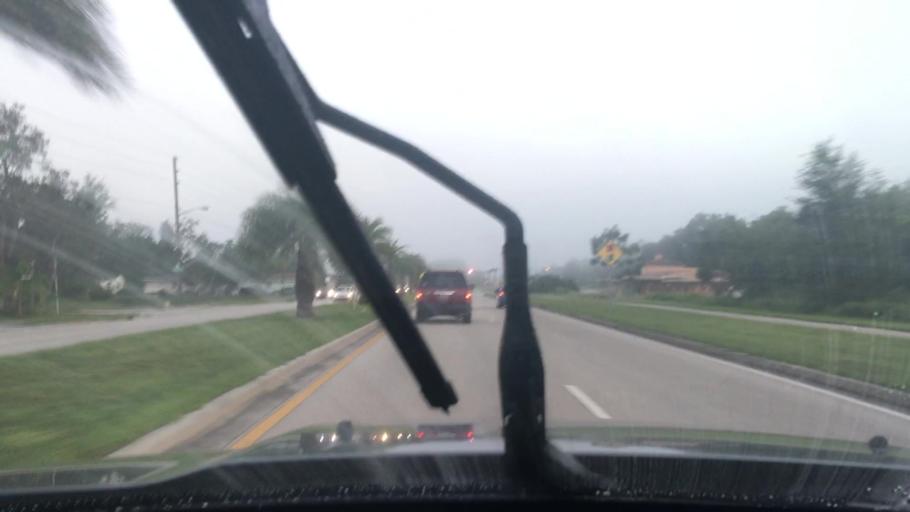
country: US
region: Florida
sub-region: Highlands County
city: Sebring
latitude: 27.4952
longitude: -81.4342
